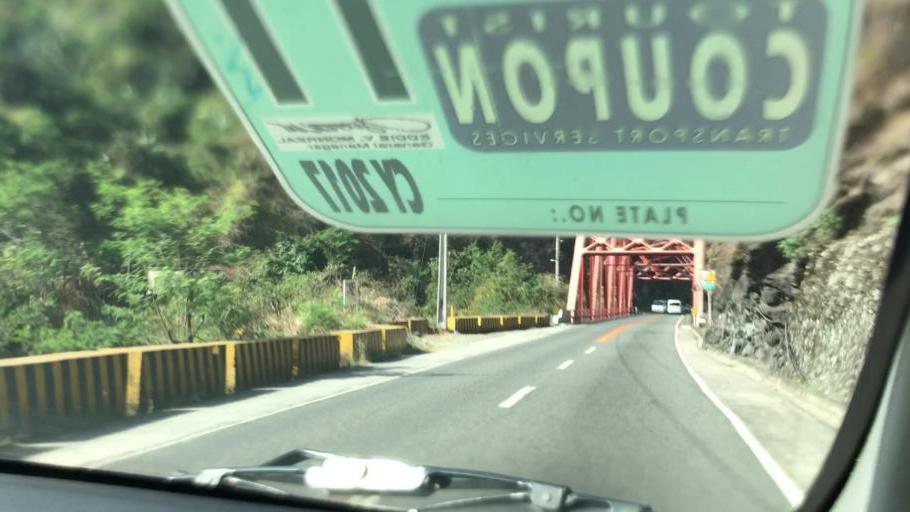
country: PH
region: Cordillera
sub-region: Province of Benguet
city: Tuba
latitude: 16.3196
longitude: 120.6150
